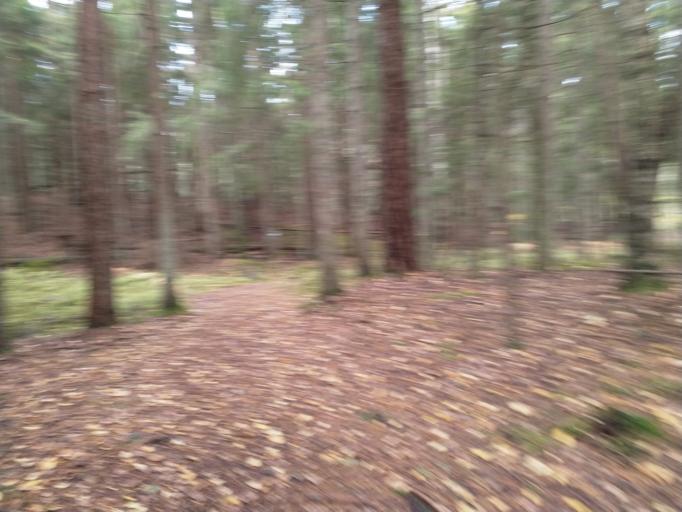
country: LV
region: Dundaga
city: Dundaga
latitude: 57.6468
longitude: 22.2591
